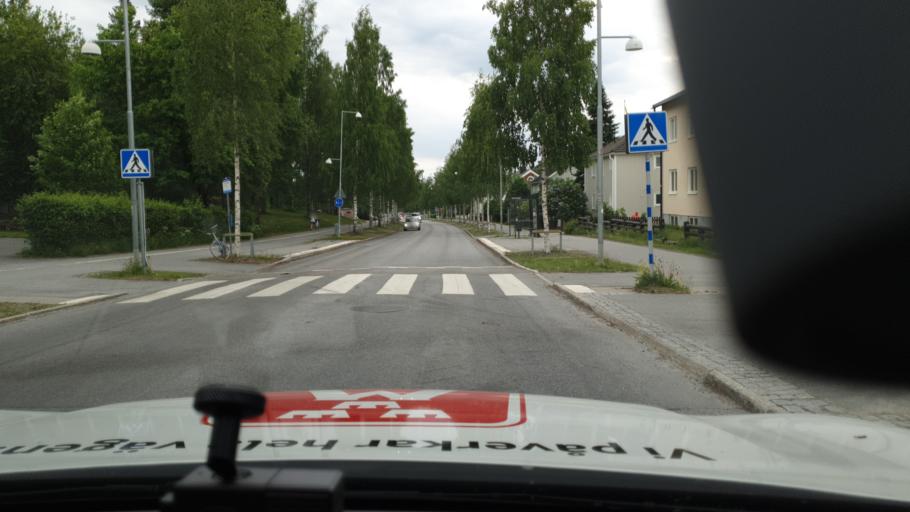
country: SE
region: Vaesterbotten
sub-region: Umea Kommun
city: Umea
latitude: 63.8427
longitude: 20.2877
